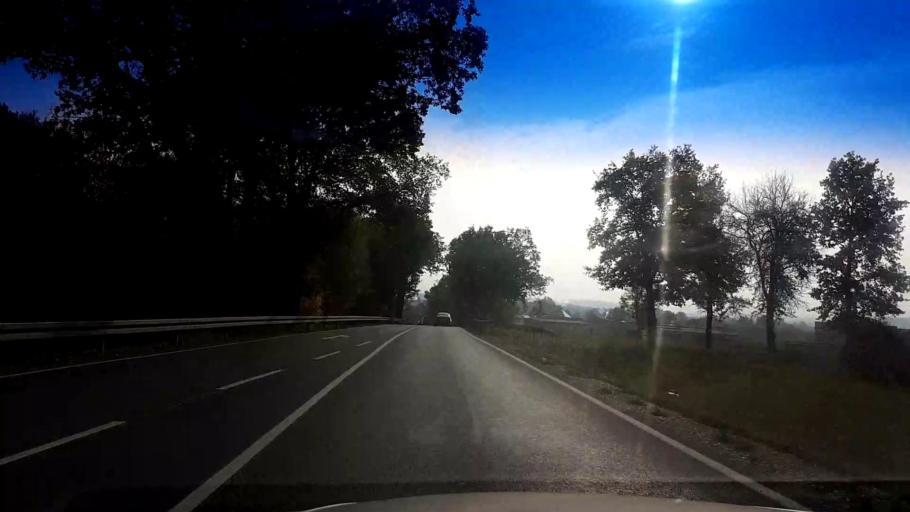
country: DE
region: Bavaria
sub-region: Upper Franconia
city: Himmelkron
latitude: 50.0585
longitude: 11.6075
